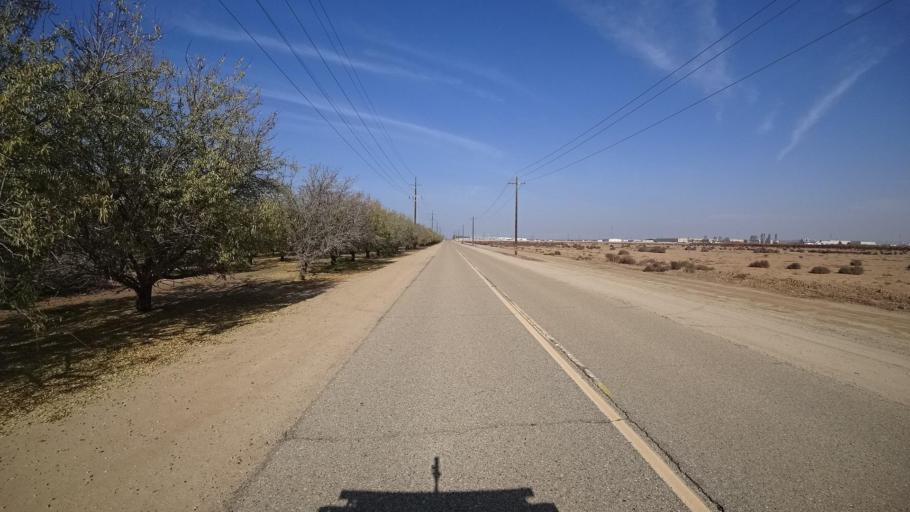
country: US
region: California
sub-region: Kern County
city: Rosedale
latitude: 35.4948
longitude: -119.1519
